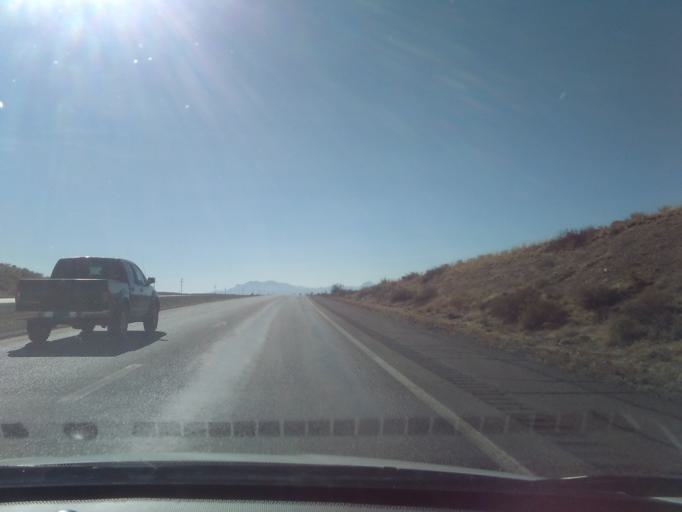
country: US
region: New Mexico
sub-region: Socorro County
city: Socorro
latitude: 34.3279
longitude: -106.8808
